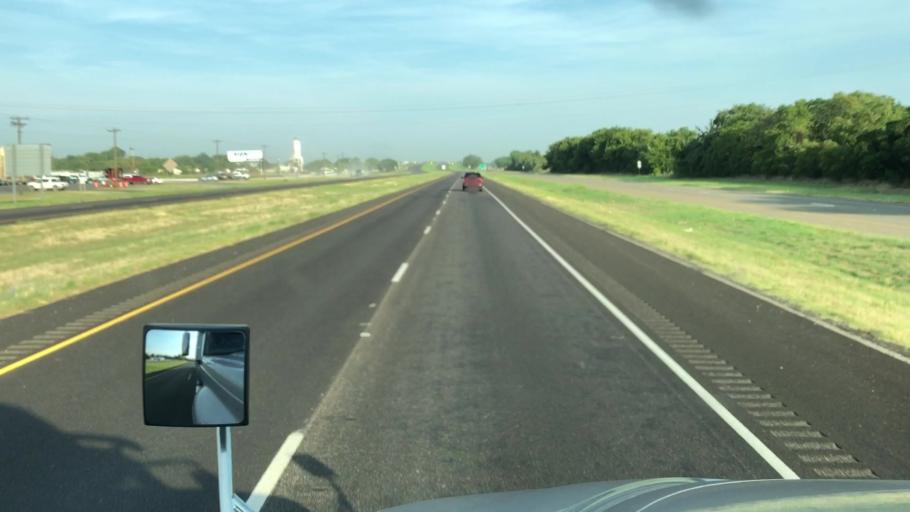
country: US
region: Texas
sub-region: McLennan County
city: Bellmead
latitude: 31.5508
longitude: -97.0809
